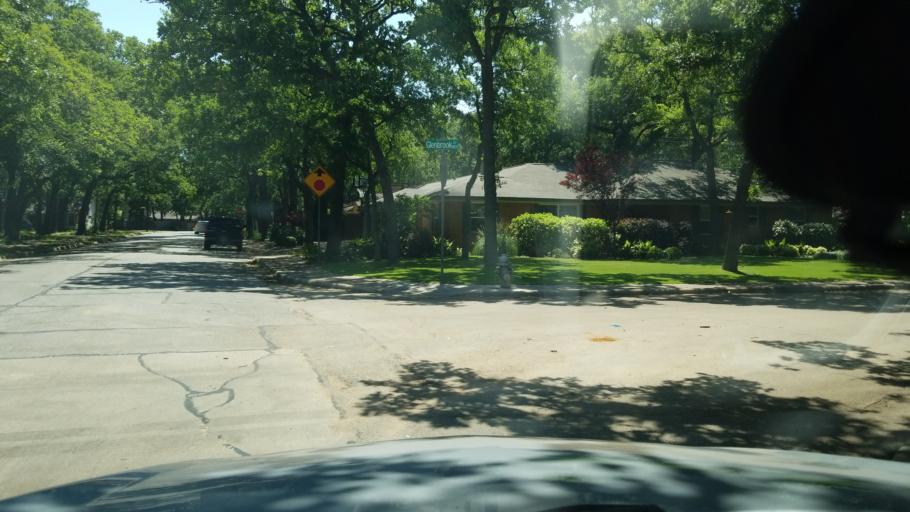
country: US
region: Texas
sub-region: Dallas County
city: Irving
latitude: 32.8338
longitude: -96.9554
